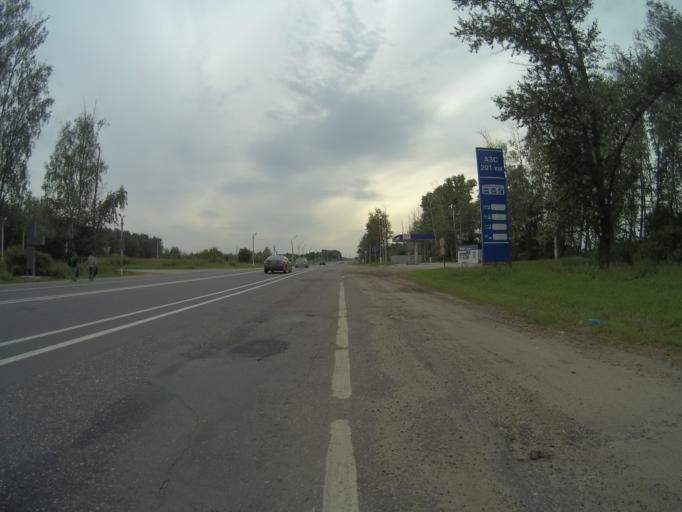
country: RU
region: Vladimir
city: Orgtrud
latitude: 56.2100
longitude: 40.5991
